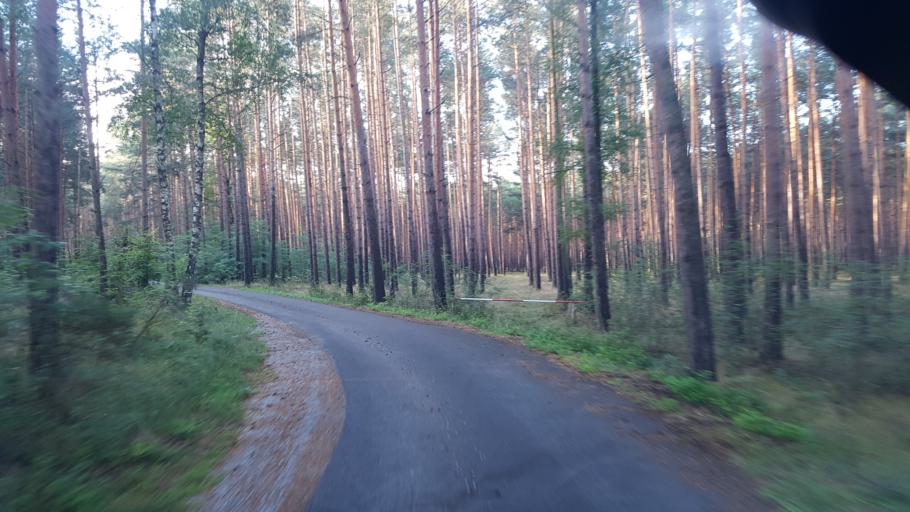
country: DE
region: Brandenburg
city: Bronkow
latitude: 51.6717
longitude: 13.8912
